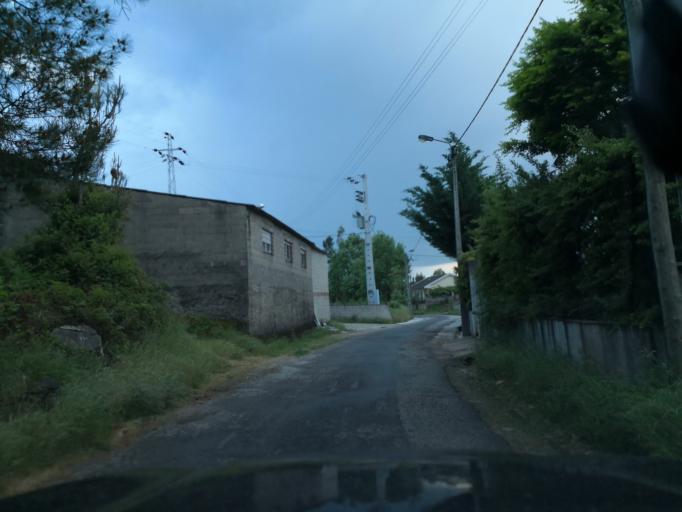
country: PT
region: Vila Real
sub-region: Vila Real
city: Vila Real
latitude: 41.3495
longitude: -7.7234
